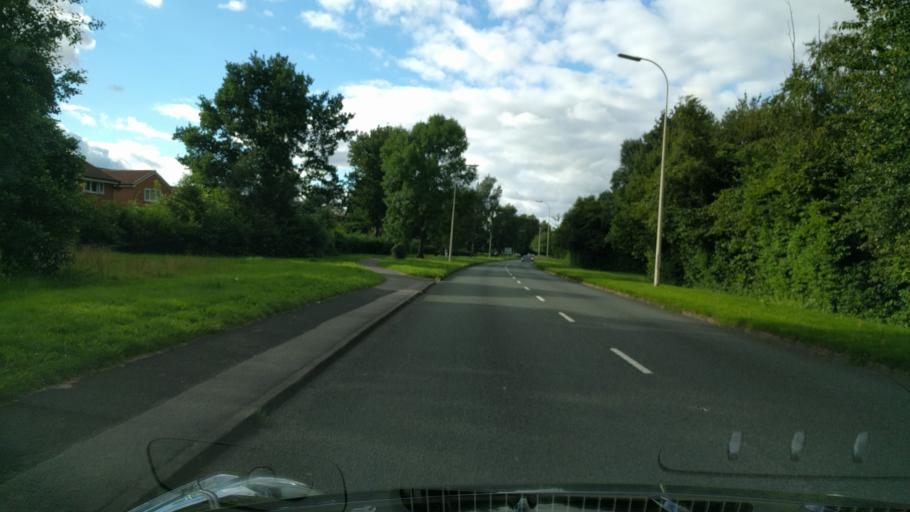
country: GB
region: England
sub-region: Warrington
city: Croft
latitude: 53.4174
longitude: -2.5666
